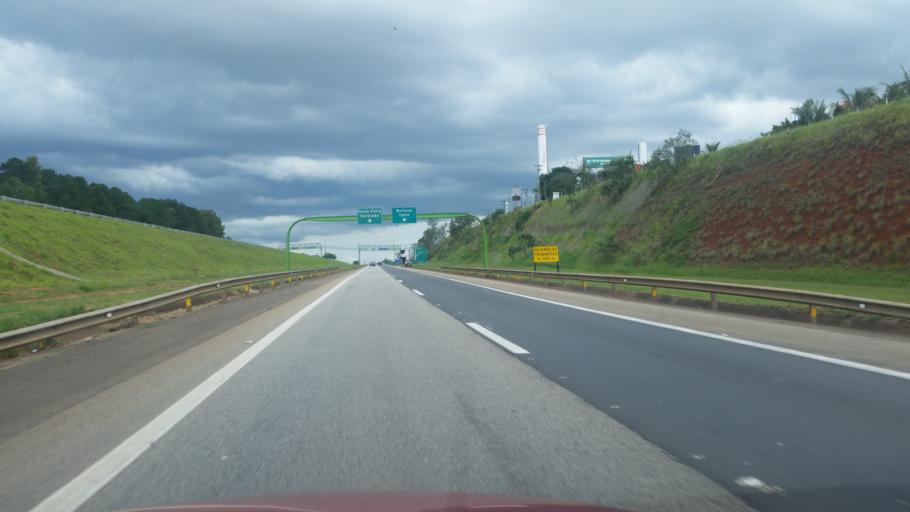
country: BR
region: Sao Paulo
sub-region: Boituva
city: Boituva
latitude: -23.2950
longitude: -47.6890
